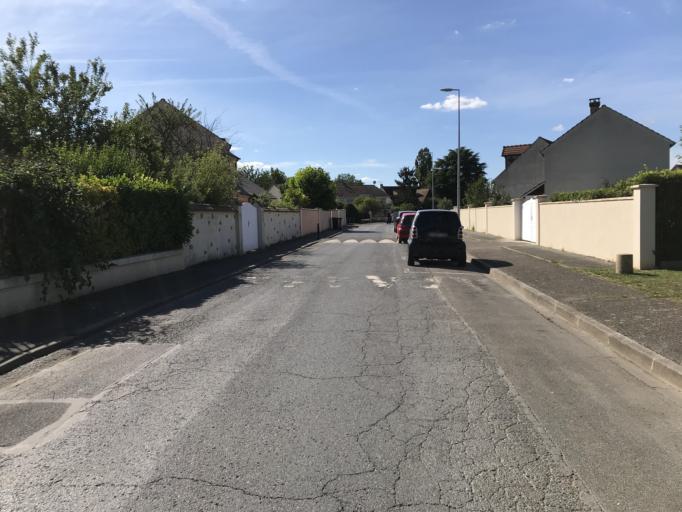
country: FR
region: Ile-de-France
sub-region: Departement de l'Essonne
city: Fleury-Merogis
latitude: 48.6306
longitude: 2.3650
